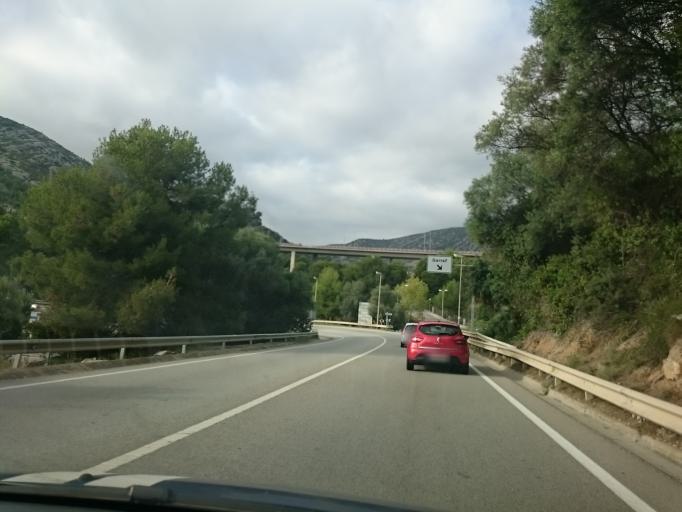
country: ES
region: Catalonia
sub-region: Provincia de Barcelona
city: Castelldefels
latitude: 41.2570
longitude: 1.9051
